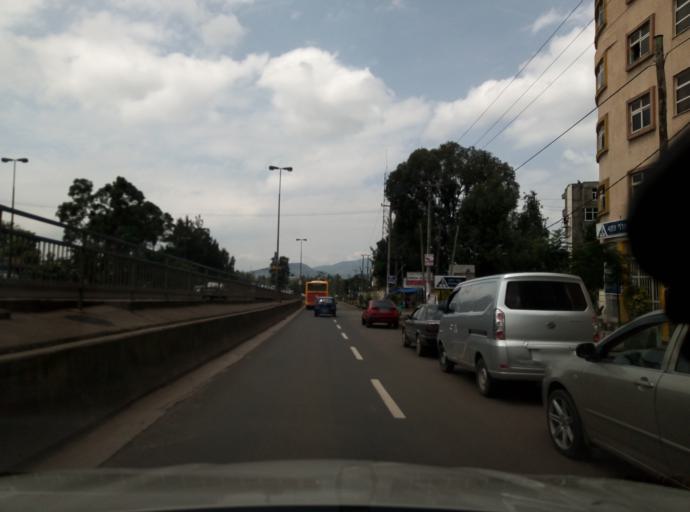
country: ET
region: Adis Abeba
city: Addis Ababa
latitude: 8.9970
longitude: 38.7184
